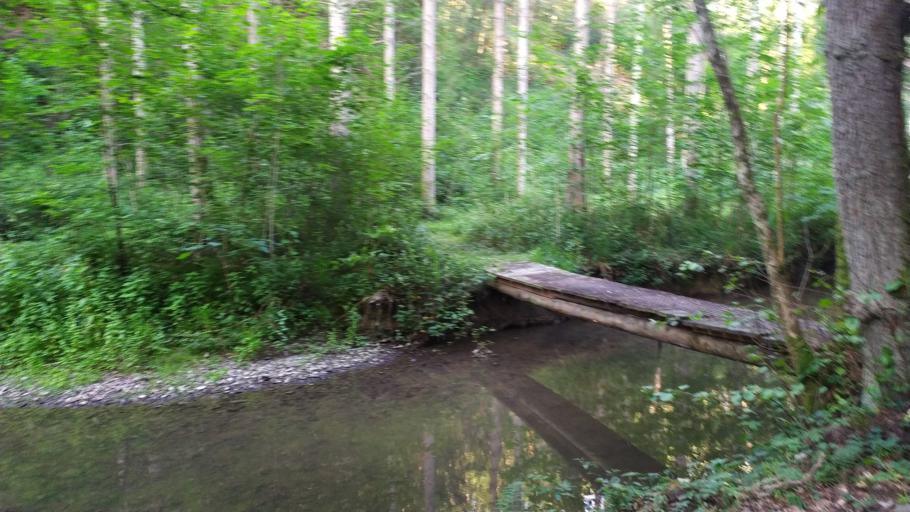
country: BE
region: Wallonia
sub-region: Province de Namur
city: Houyet
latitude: 50.2064
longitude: 5.0386
